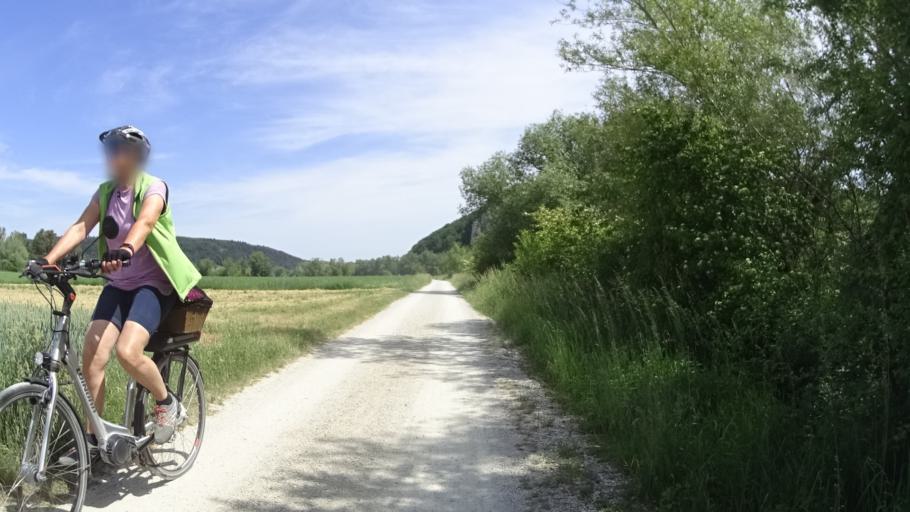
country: DE
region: Bavaria
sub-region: Lower Bavaria
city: Saal
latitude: 48.9097
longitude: 11.9676
